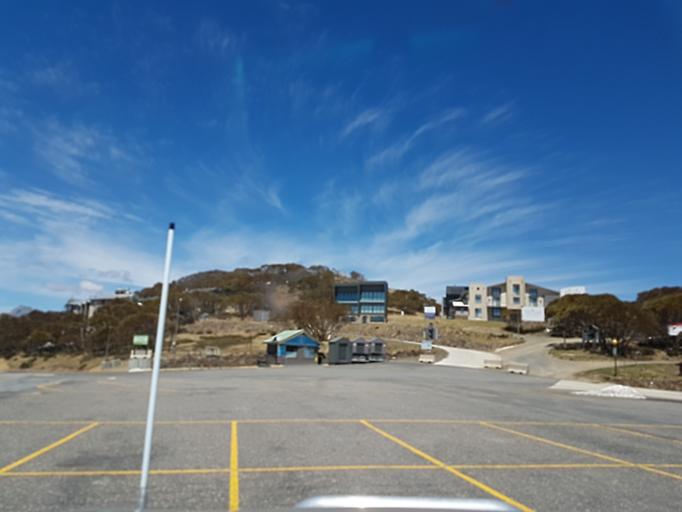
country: AU
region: Victoria
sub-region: Alpine
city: Mount Beauty
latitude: -36.9828
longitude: 147.1426
